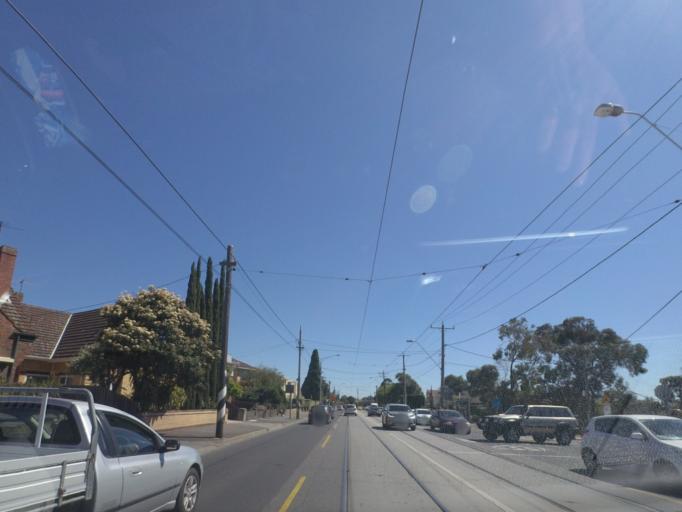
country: AU
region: Victoria
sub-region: Moreland
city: Coburg North
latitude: -37.7325
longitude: 144.9647
